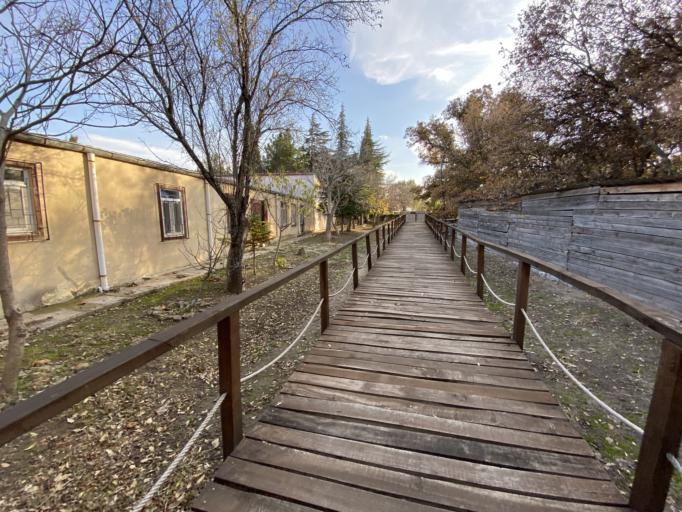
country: TR
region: Canakkale
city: Intepe
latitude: 39.9574
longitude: 26.2400
